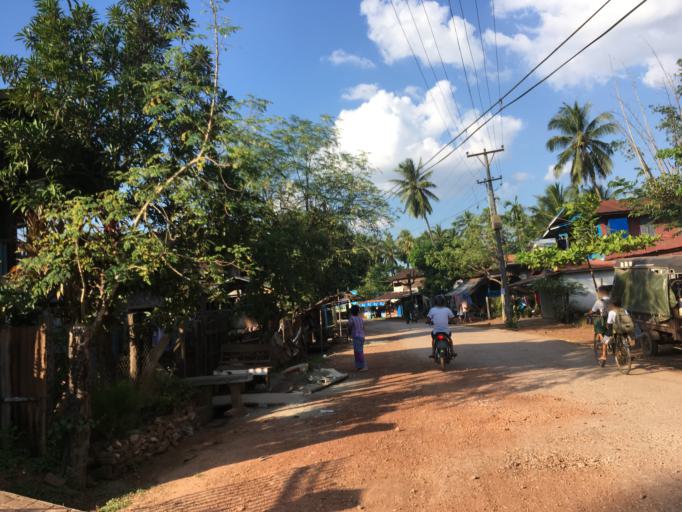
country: MM
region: Mon
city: Mawlamyine
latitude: 16.4384
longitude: 97.6208
